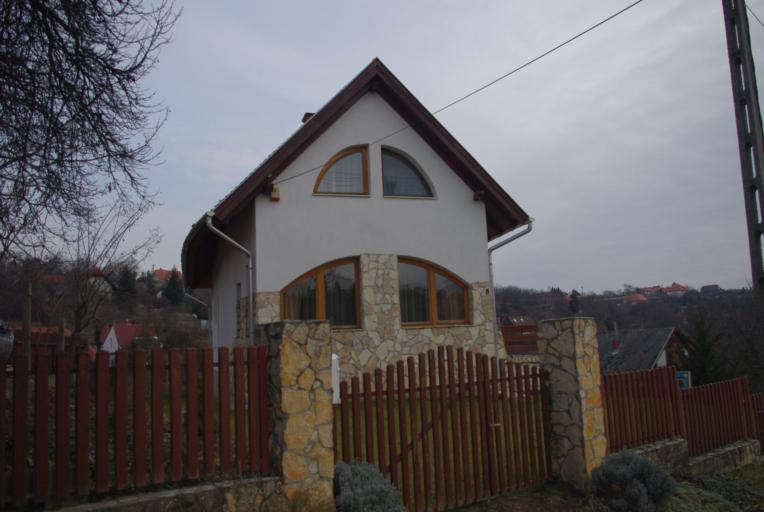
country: HU
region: Fejer
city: Gardony
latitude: 47.2461
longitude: 18.5958
